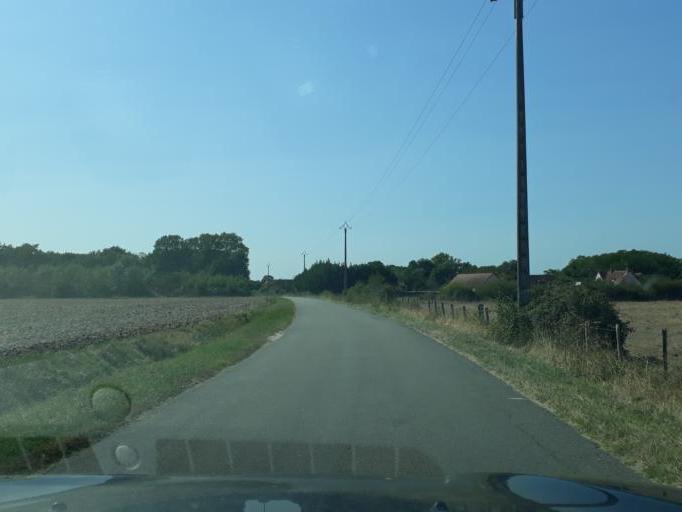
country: FR
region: Centre
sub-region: Departement du Loir-et-Cher
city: Gievres
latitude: 47.2595
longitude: 1.6902
